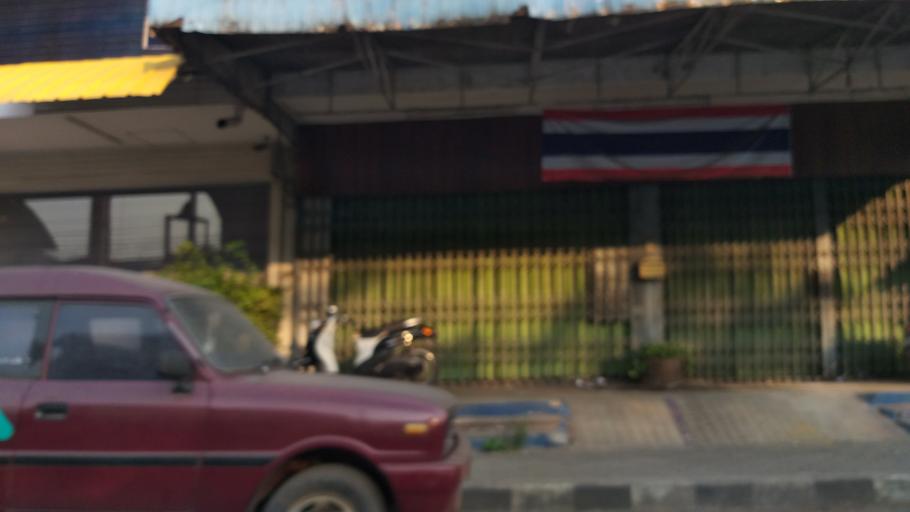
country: TH
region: Khon Kaen
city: Khon Kaen
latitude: 16.4183
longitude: 102.8327
